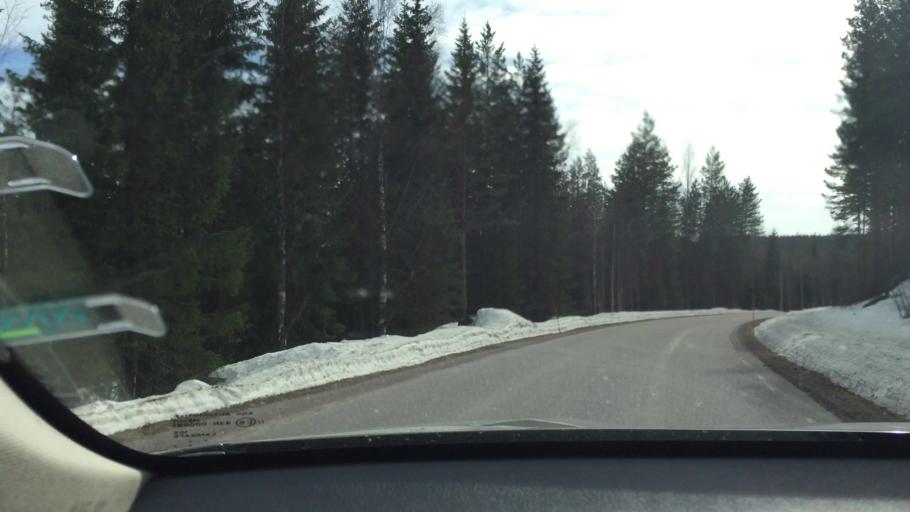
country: NO
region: Hedmark
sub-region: Trysil
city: Innbygda
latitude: 61.0687
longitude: 12.5562
